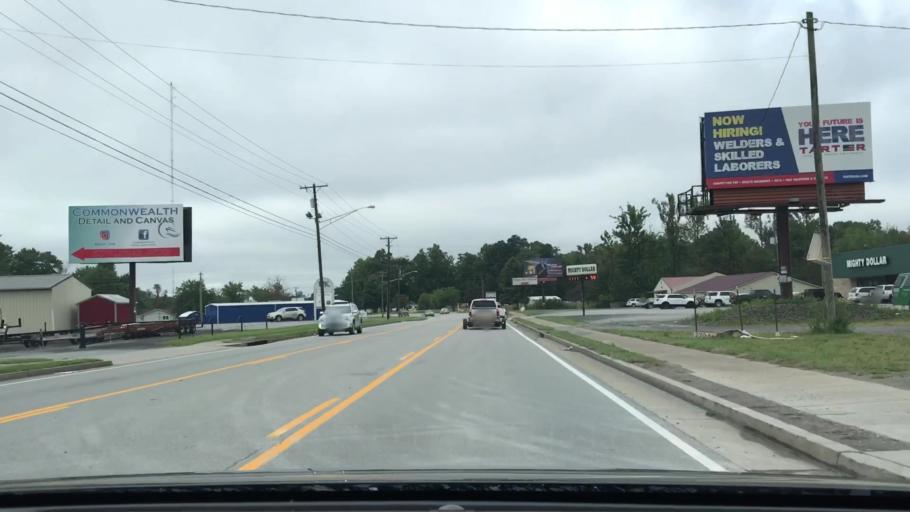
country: US
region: Kentucky
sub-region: Russell County
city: Russell Springs
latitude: 37.0288
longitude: -85.0772
